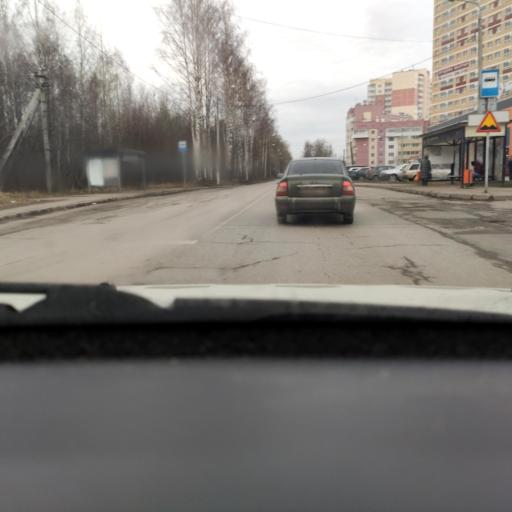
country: RU
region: Perm
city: Polazna
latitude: 58.1331
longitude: 56.4028
